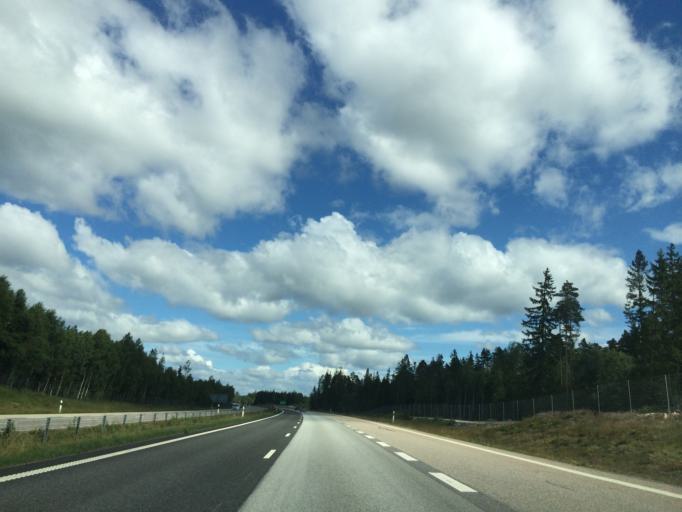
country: SE
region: Kronoberg
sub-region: Markaryds Kommun
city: Stromsnasbruk
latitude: 56.5648
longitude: 13.7219
